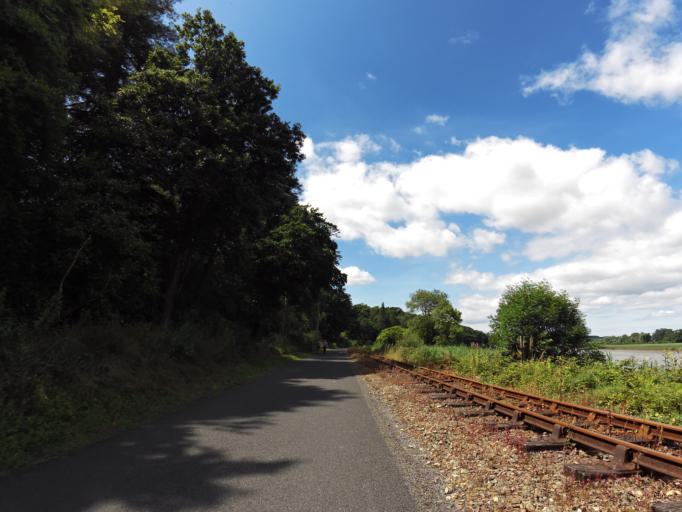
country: IE
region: Leinster
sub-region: Kilkenny
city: Mooncoin
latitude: 52.2420
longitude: -7.2175
